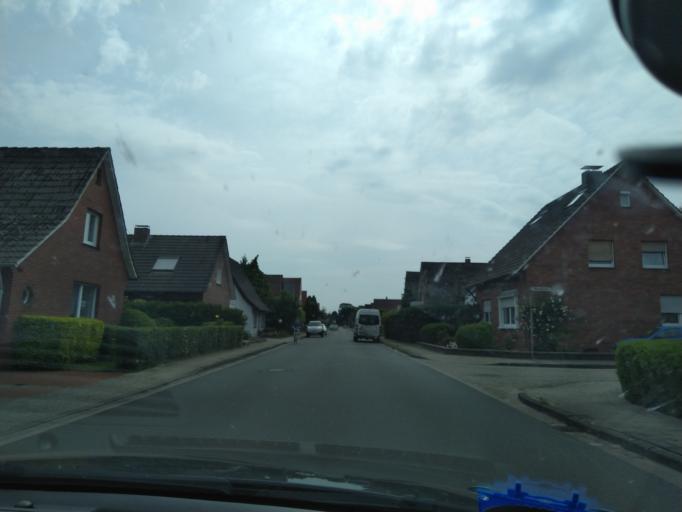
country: DE
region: Lower Saxony
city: Nordhorn
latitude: 52.4562
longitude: 7.0621
